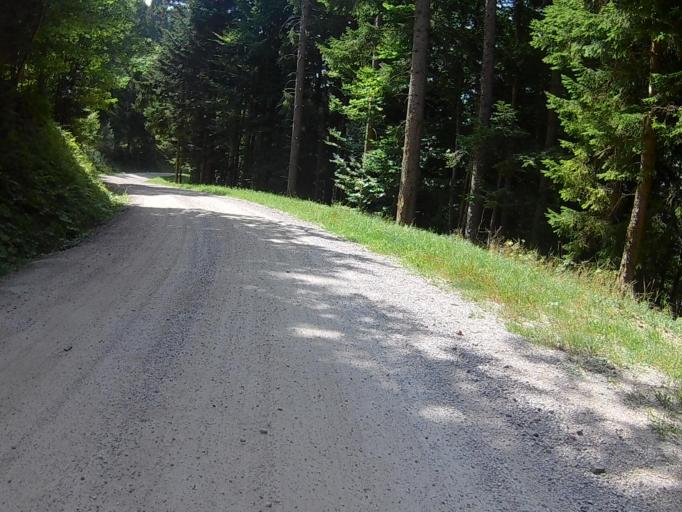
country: SI
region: Ruse
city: Ruse
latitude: 46.5023
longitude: 15.5351
